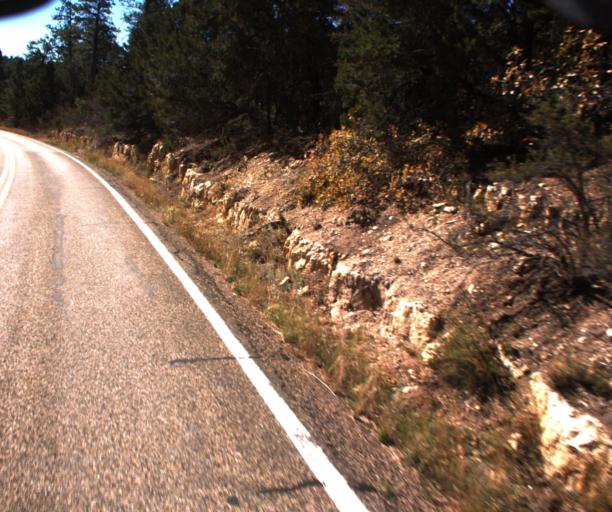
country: US
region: Arizona
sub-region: Coconino County
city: Fredonia
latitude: 36.7793
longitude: -112.2566
